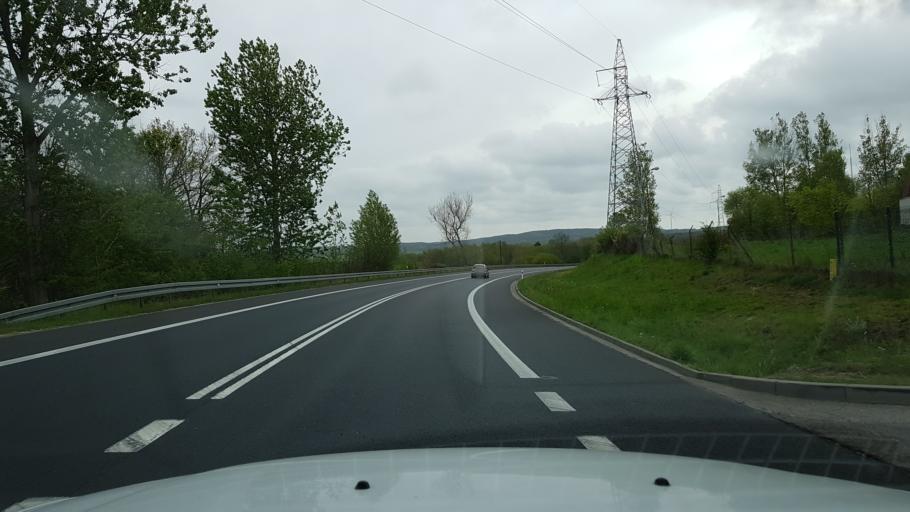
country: PL
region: West Pomeranian Voivodeship
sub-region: Powiat slawienski
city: Darlowo
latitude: 54.3000
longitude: 16.5075
